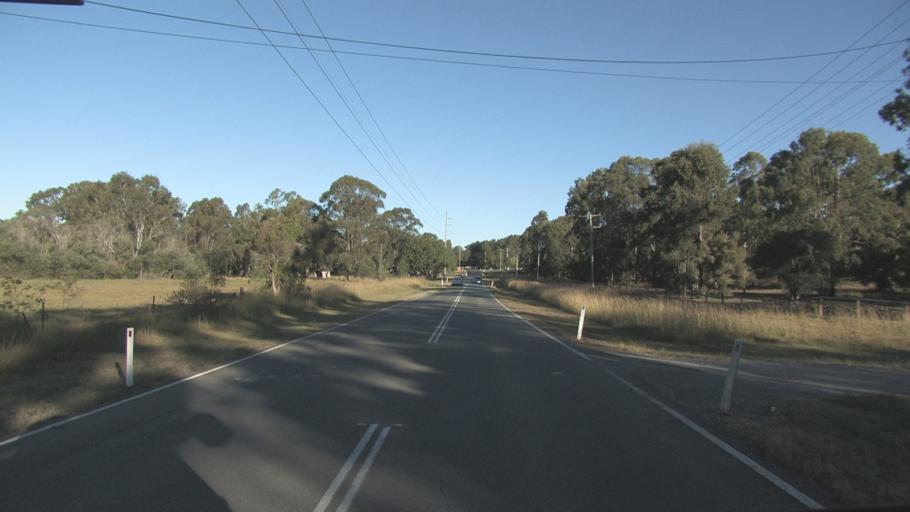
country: AU
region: Queensland
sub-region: Logan
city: Chambers Flat
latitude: -27.7407
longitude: 153.0870
